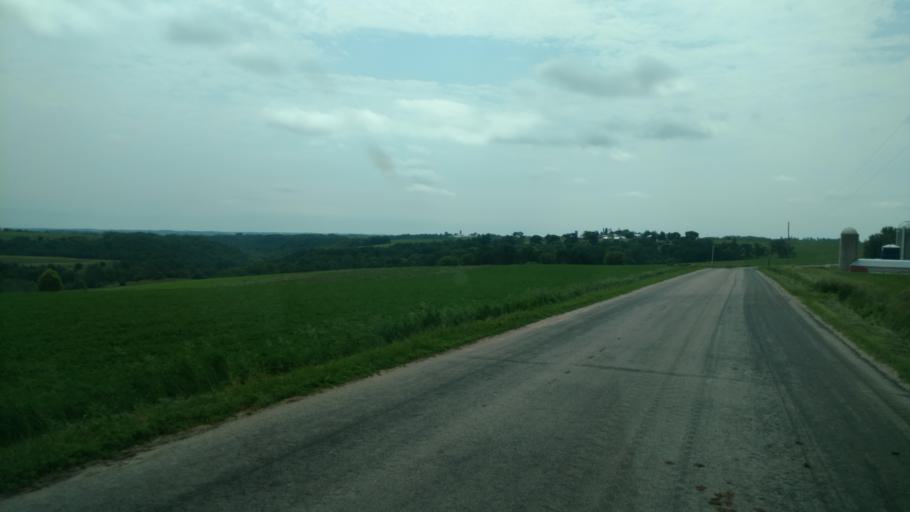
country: US
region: Wisconsin
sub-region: Monroe County
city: Cashton
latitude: 43.7792
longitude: -90.6683
